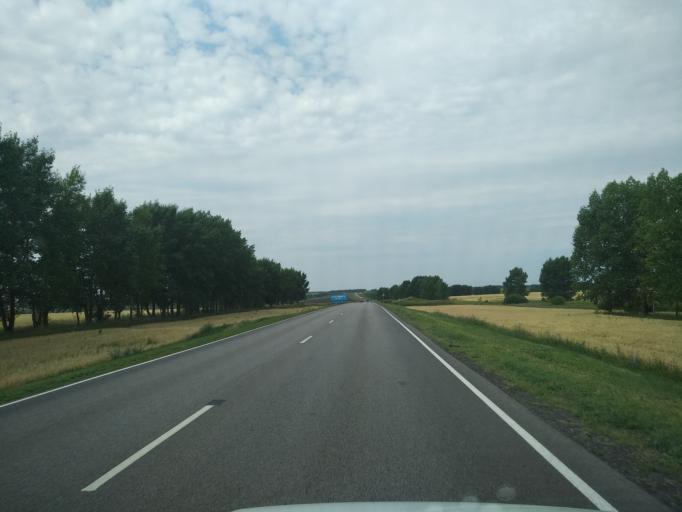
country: RU
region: Voronezj
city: Pereleshinskiy
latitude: 51.8616
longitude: 40.3581
